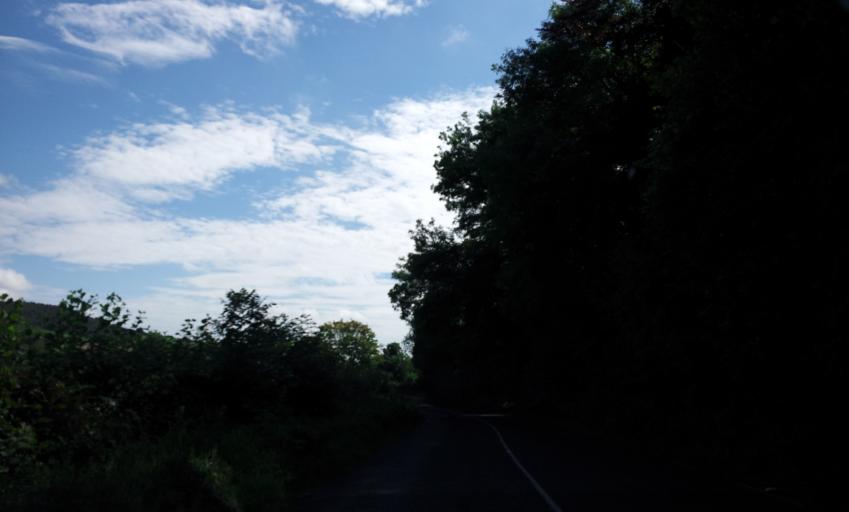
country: IE
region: Leinster
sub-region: Laois
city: Portlaoise
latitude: 53.0120
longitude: -7.2443
